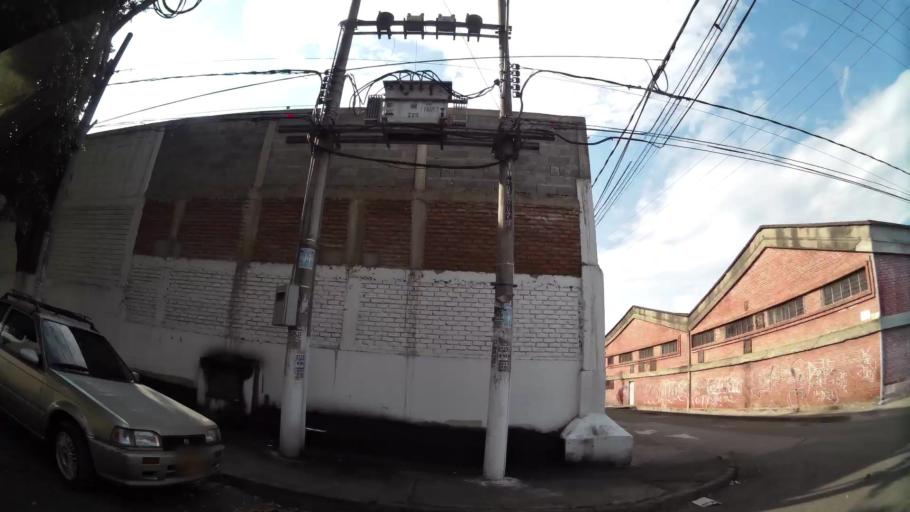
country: CO
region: Valle del Cauca
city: Cali
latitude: 3.4696
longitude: -76.5133
